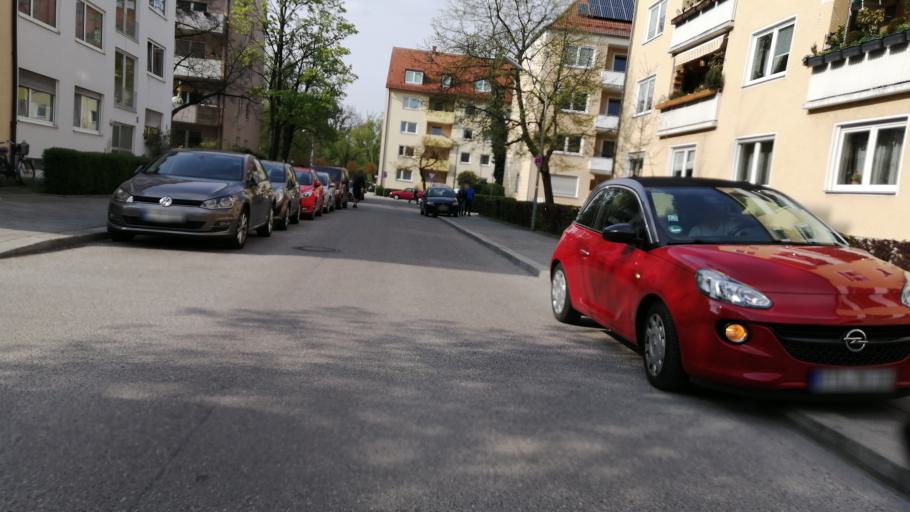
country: DE
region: Bavaria
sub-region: Upper Bavaria
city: Munich
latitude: 48.1837
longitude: 11.5699
